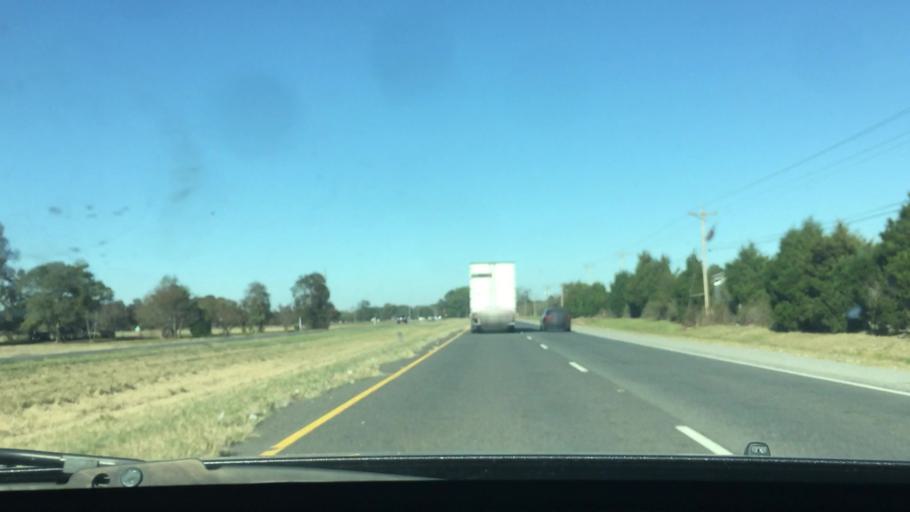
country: US
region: Louisiana
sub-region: Richland Parish
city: Rayville
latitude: 32.3737
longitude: -91.7707
